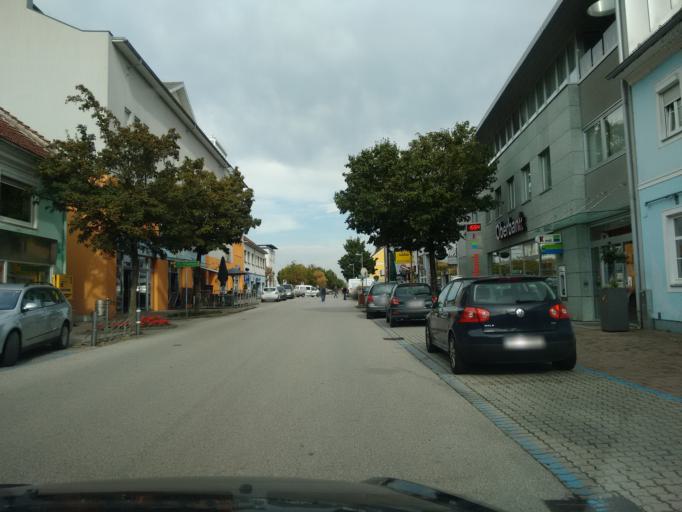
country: AT
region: Upper Austria
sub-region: Wels-Land
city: Marchtrenk
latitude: 48.1905
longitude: 14.1135
